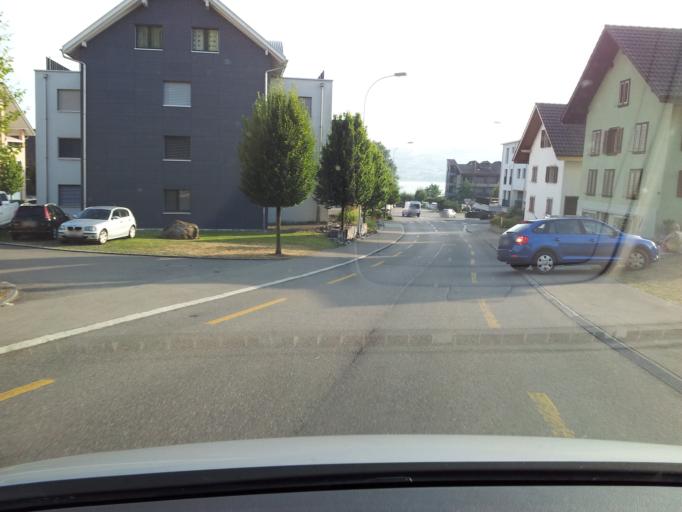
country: CH
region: Lucerne
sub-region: Sursee District
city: Eich
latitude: 47.1514
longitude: 8.1687
